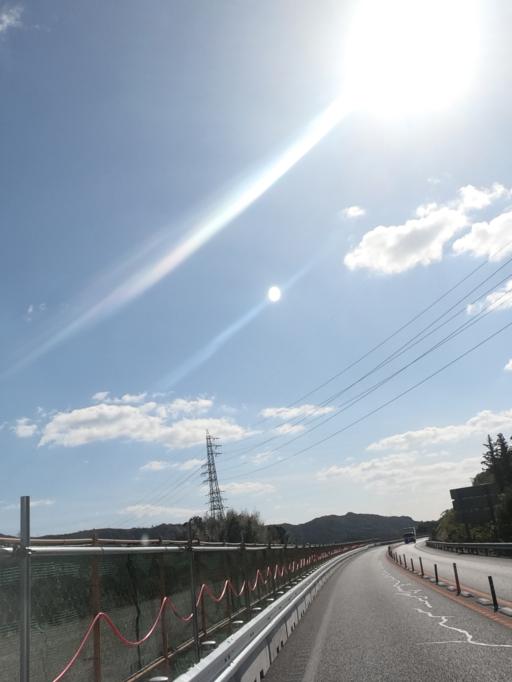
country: JP
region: Wakayama
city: Gobo
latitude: 33.8400
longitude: 135.2204
